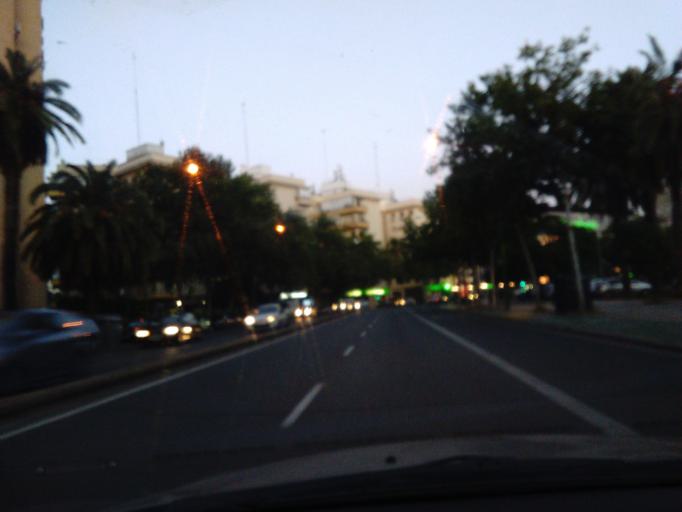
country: ES
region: Andalusia
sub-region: Provincia de Sevilla
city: Sevilla
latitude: 37.3887
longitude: -5.9732
